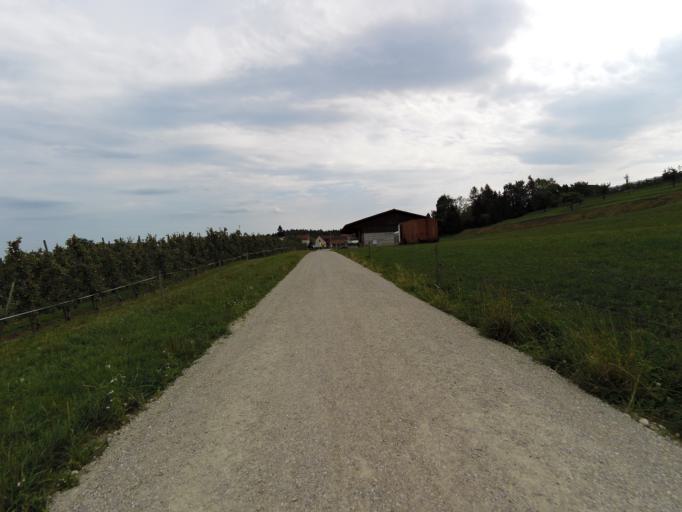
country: CH
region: Thurgau
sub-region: Kreuzlingen District
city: Ermatingen
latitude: 47.6635
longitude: 9.0645
